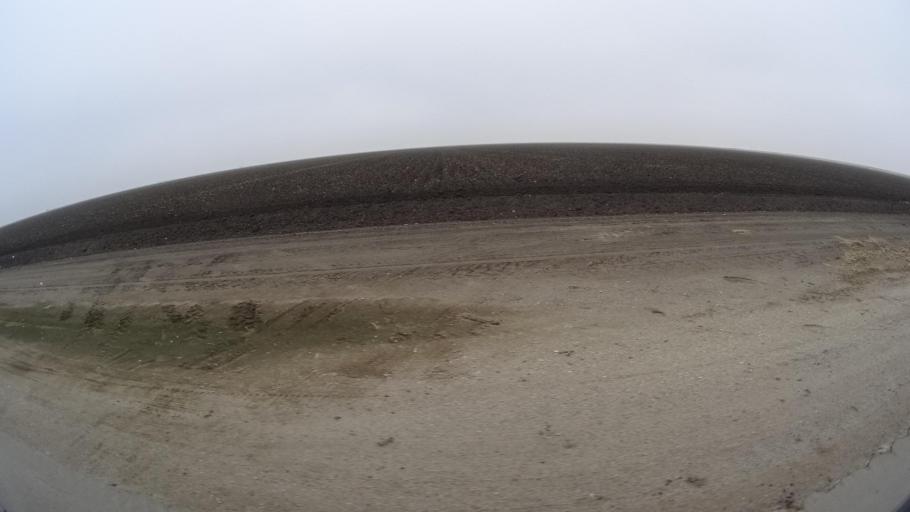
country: US
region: California
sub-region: Kern County
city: Rosedale
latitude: 35.1944
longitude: -119.2282
